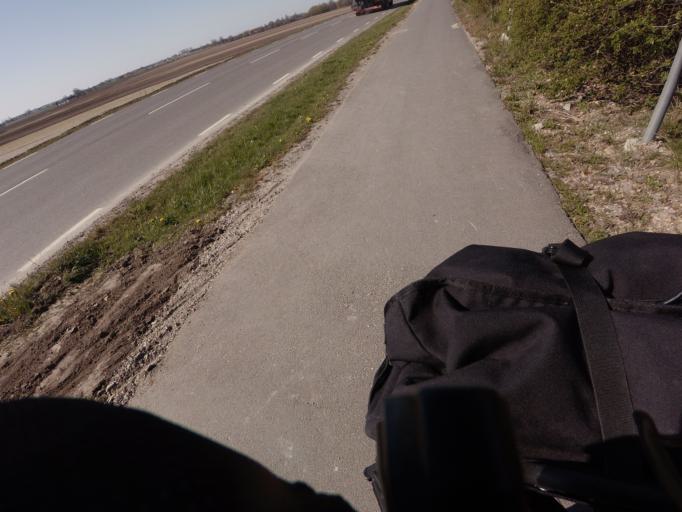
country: SE
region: Skane
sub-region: Vellinge Kommun
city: Vellinge
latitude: 55.4707
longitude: 13.0404
